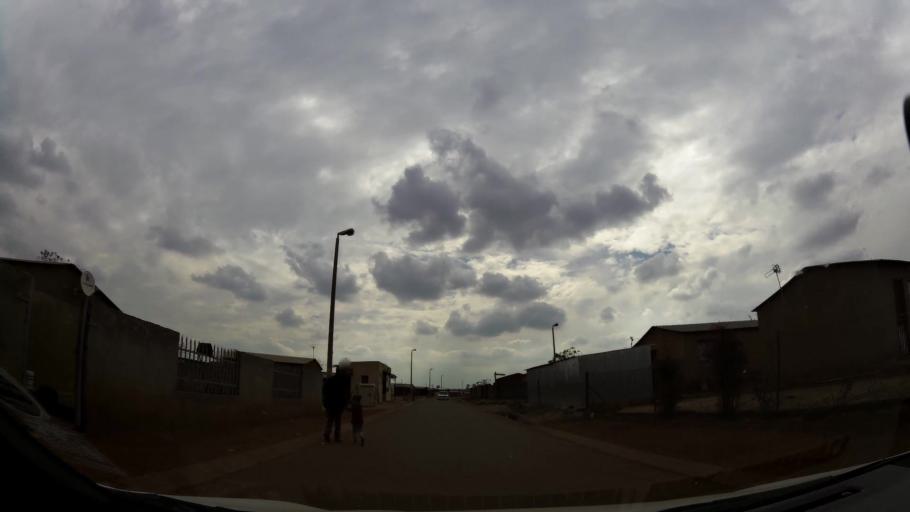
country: ZA
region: Gauteng
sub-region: Ekurhuleni Metropolitan Municipality
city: Germiston
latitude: -26.3894
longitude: 28.1183
